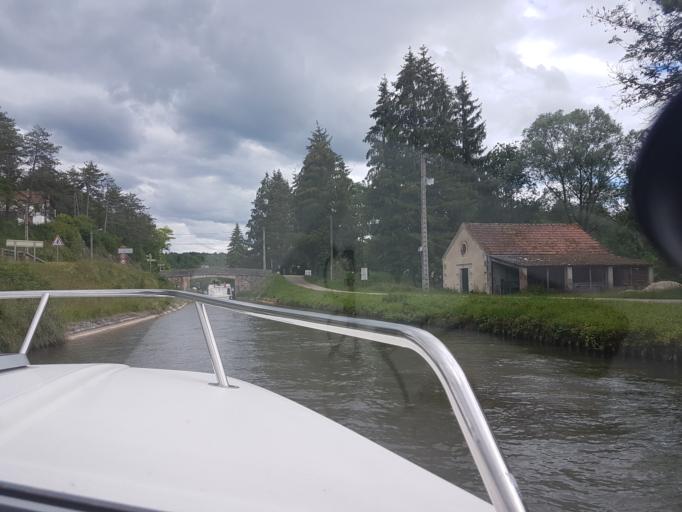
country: FR
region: Bourgogne
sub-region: Departement de l'Yonne
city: Vermenton
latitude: 47.5665
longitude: 3.6400
